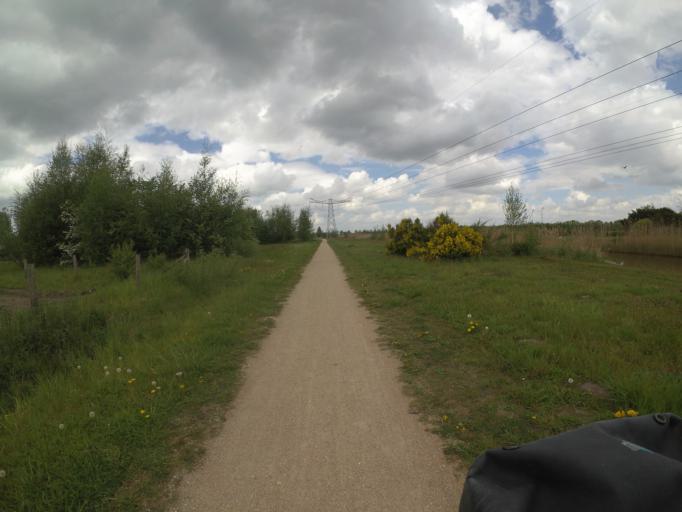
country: NL
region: North Brabant
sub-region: Gemeente Dongen
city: Dongen
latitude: 51.6350
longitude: 4.9537
